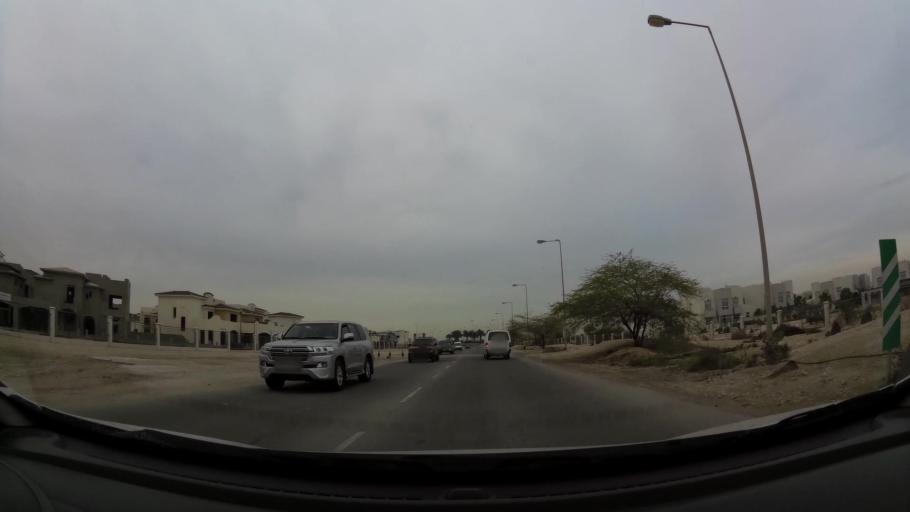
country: BH
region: Northern
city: Ar Rifa'
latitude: 26.0933
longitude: 50.5604
